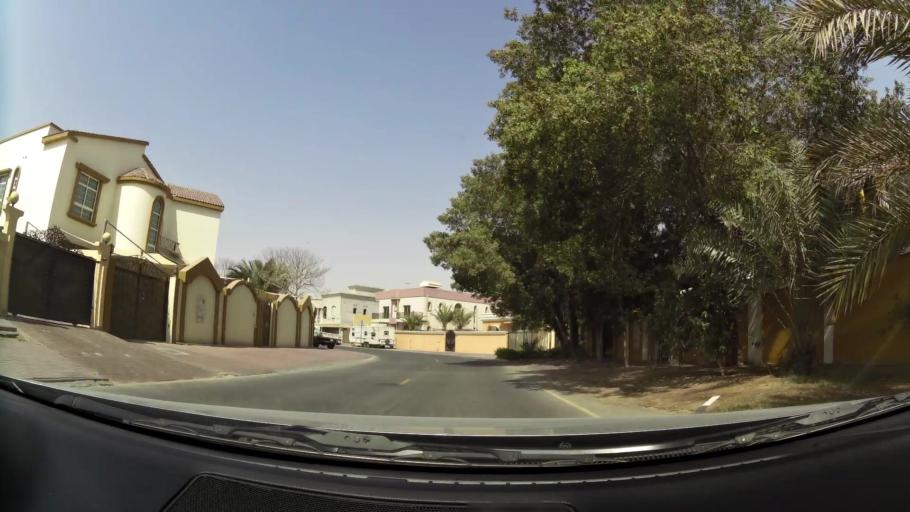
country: AE
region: Dubai
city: Dubai
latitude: 25.1651
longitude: 55.2623
